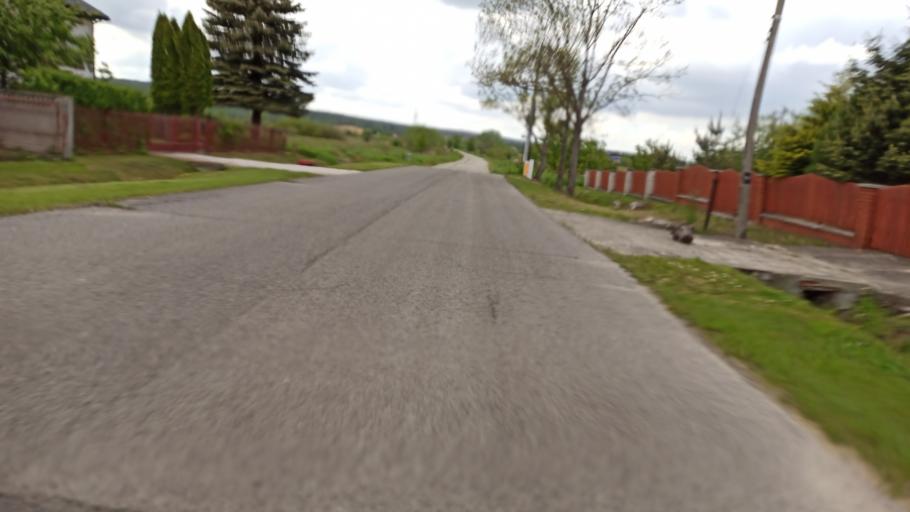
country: PL
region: Swietokrzyskie
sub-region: Powiat skarzyski
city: Skarzysko Koscielne
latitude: 51.1385
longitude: 20.9050
